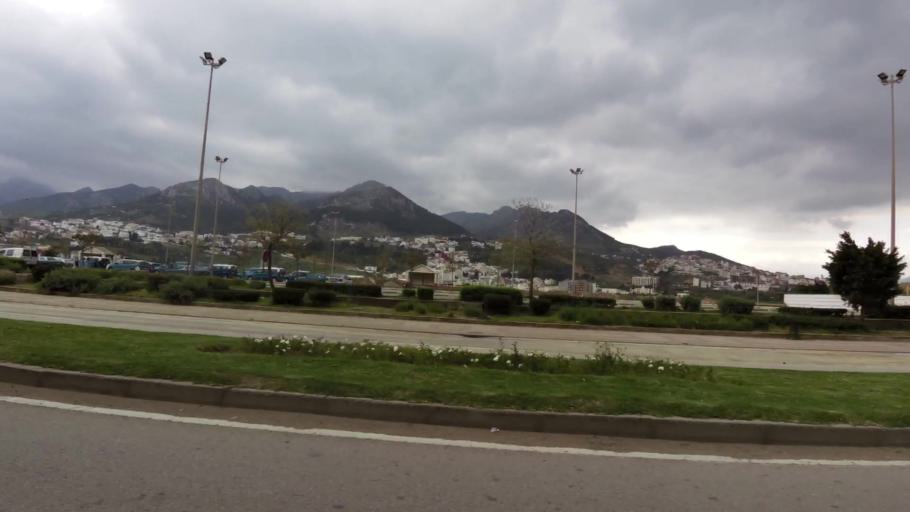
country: MA
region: Tanger-Tetouan
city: Tetouan
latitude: 35.5624
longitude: -5.3738
